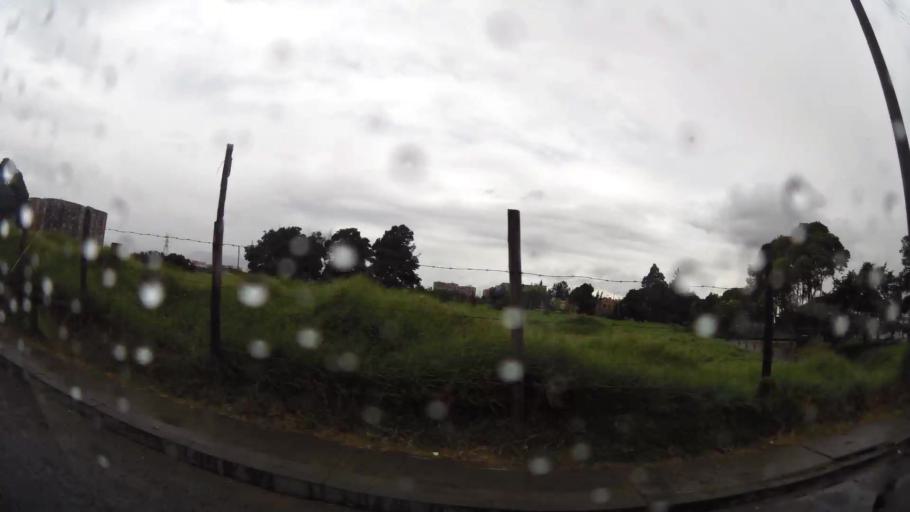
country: CO
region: Bogota D.C.
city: Bogota
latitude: 4.6623
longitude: -74.1218
